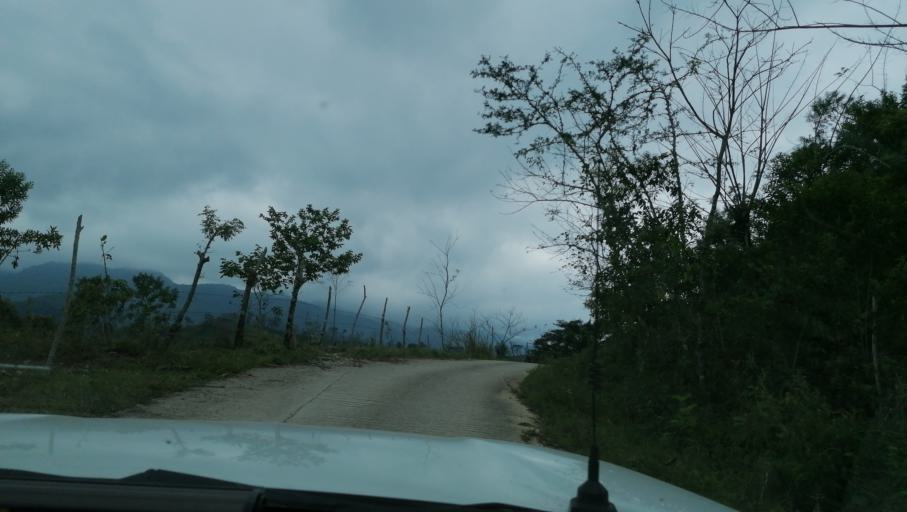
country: MX
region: Chiapas
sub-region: Ocotepec
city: San Pablo Huacano
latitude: 17.2765
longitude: -93.2336
